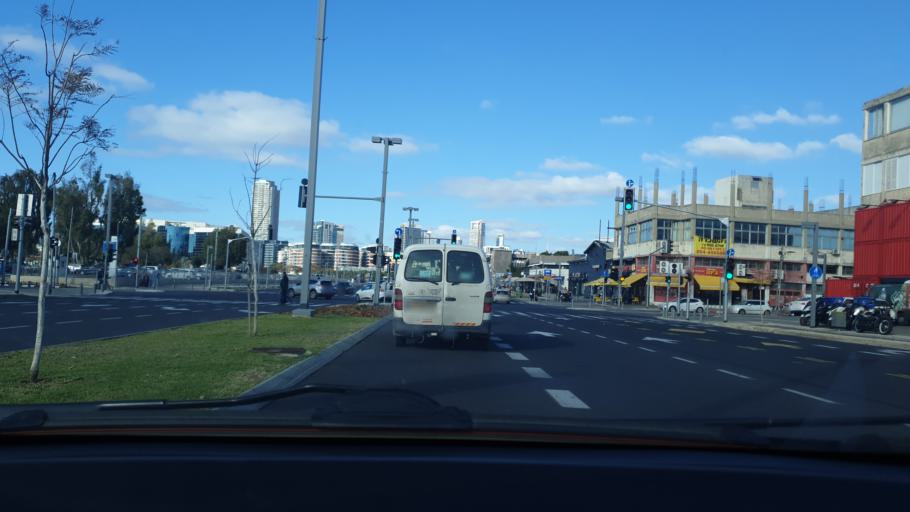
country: IL
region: Tel Aviv
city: Yafo
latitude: 32.0493
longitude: 34.7639
